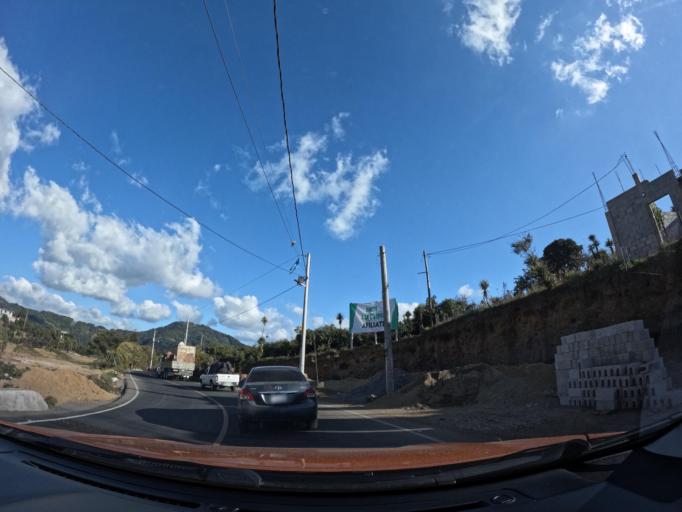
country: GT
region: Sacatepequez
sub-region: Municipio de Santa Maria de Jesus
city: Santa Maria de Jesus
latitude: 14.4877
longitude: -90.7073
